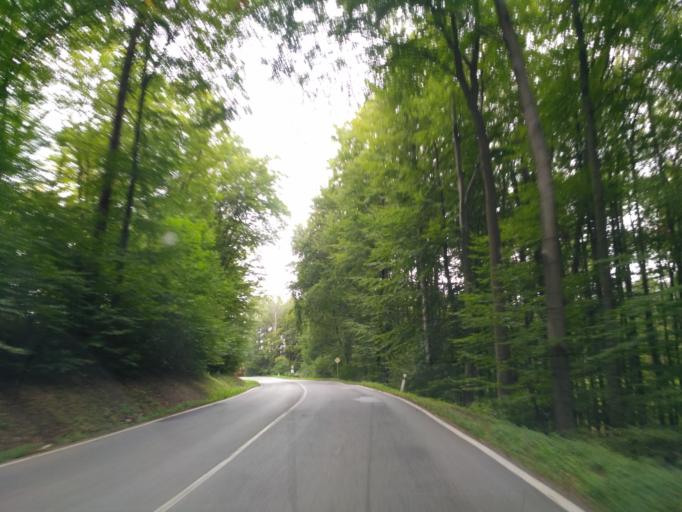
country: SK
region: Presovsky
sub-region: Okres Presov
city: Presov
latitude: 48.9888
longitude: 21.1828
